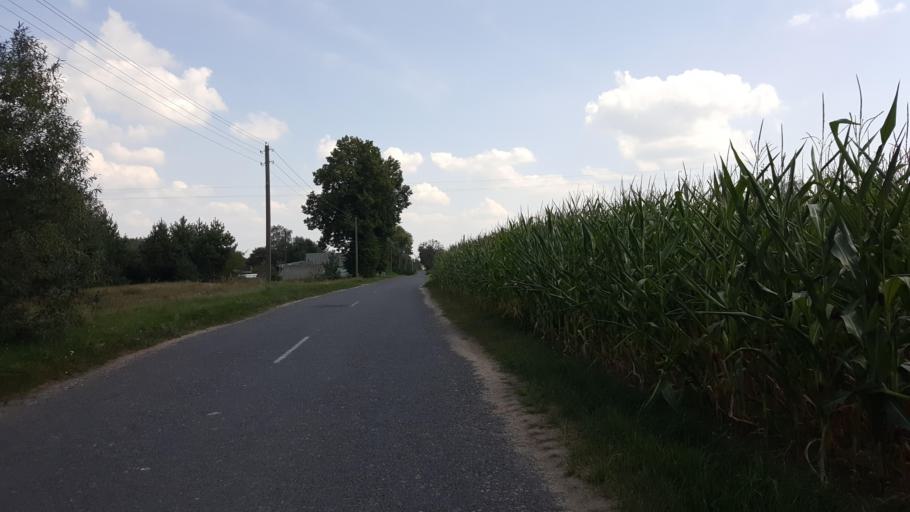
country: PL
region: Podlasie
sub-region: Powiat hajnowski
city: Czeremcha
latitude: 52.5136
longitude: 23.5392
